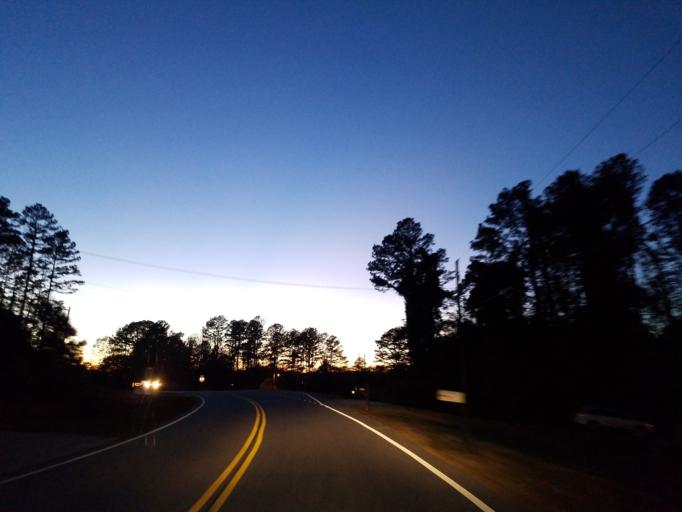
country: US
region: Georgia
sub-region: Dawson County
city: Dawsonville
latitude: 34.3326
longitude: -84.1052
